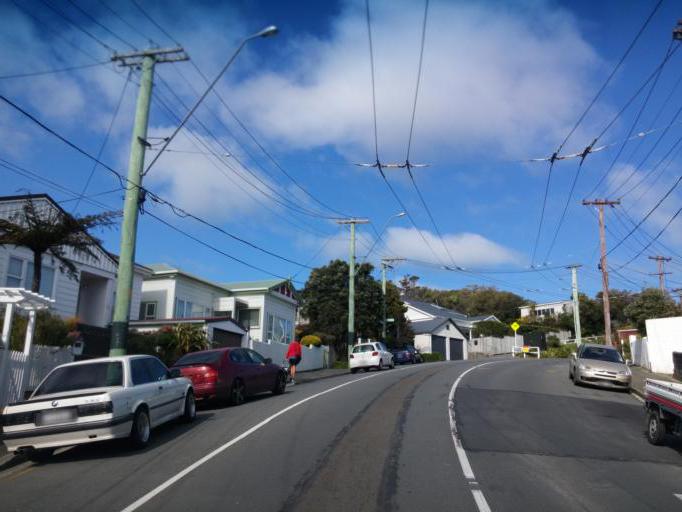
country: NZ
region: Wellington
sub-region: Wellington City
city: Brooklyn
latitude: -41.3099
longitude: 174.7660
